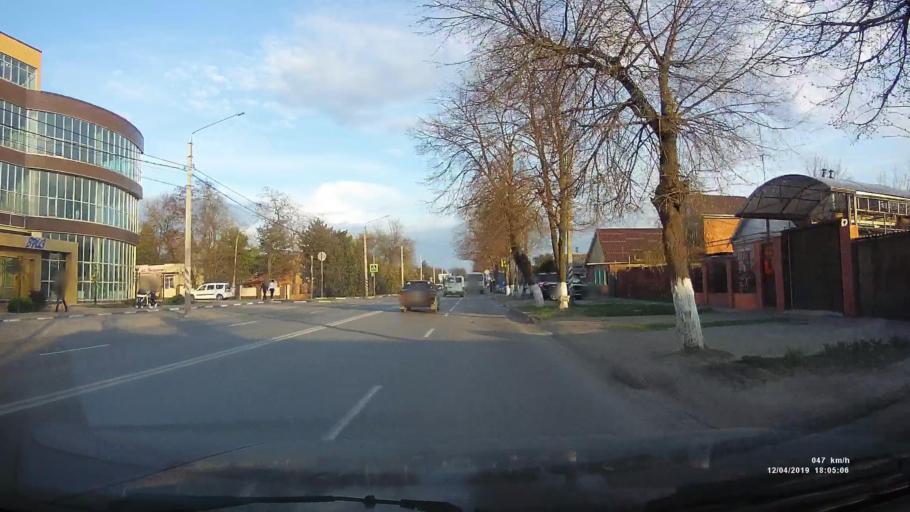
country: RU
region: Rostov
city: Azov
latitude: 47.1015
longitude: 39.4381
